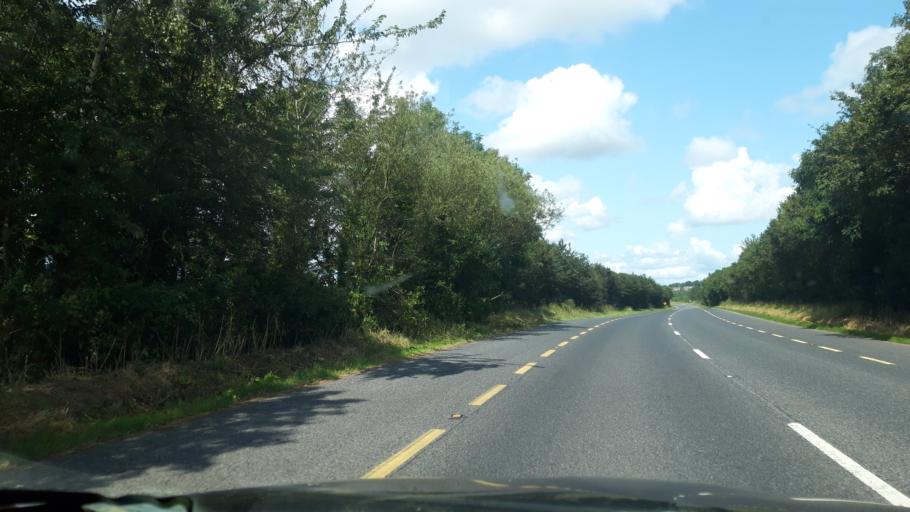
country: IE
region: Munster
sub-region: Waterford
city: Waterford
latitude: 52.2760
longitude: -7.0547
